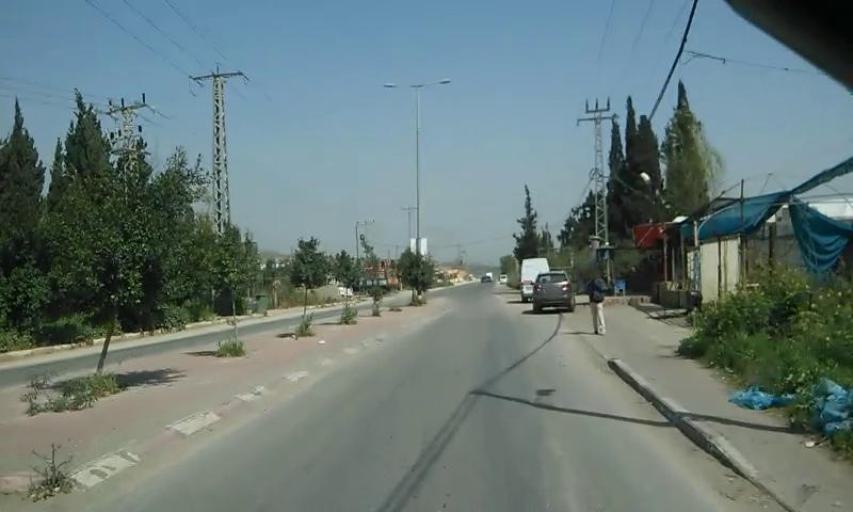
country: PS
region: West Bank
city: Ash Shuhada'
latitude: 32.4314
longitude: 35.2673
